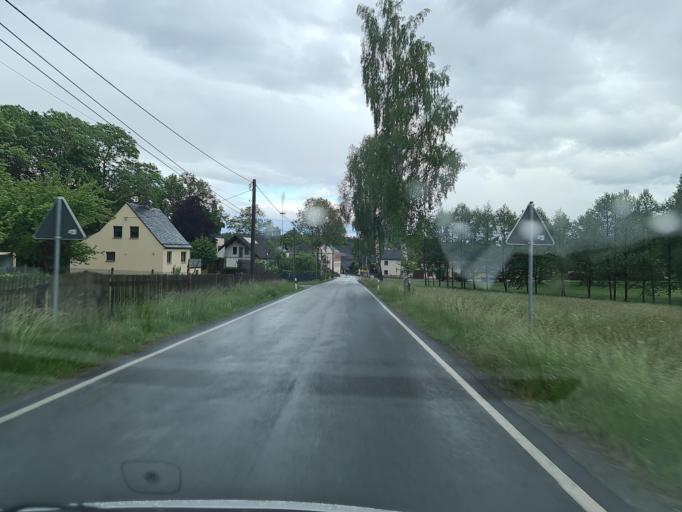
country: DE
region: Saxony
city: Muhltroff
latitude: 50.5028
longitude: 11.9073
